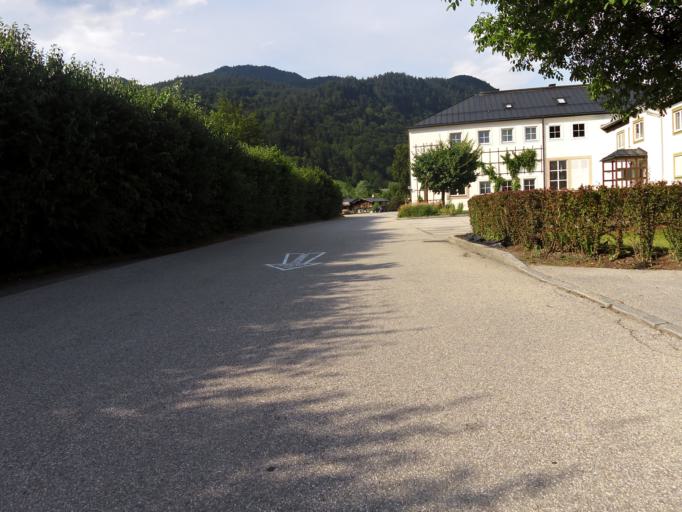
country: DE
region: Bavaria
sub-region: Upper Bavaria
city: Berchtesgaden
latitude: 47.6381
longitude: 13.0164
